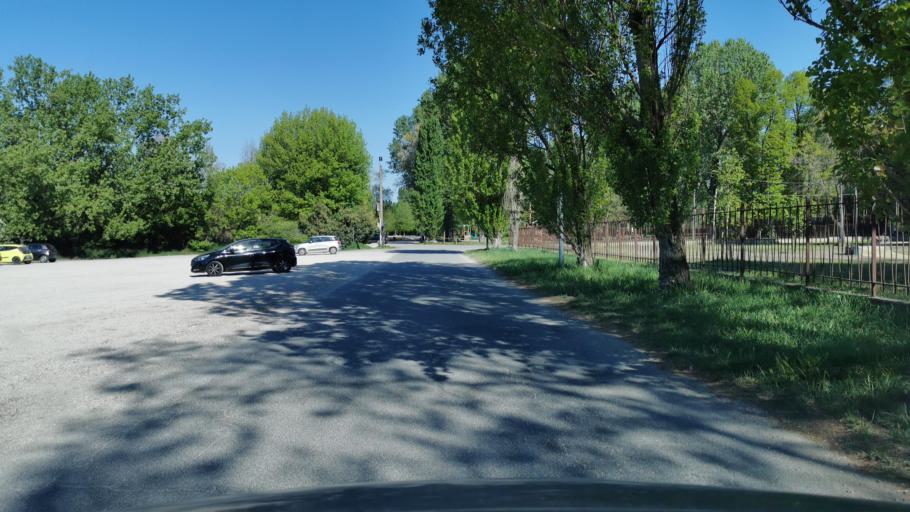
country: IT
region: Lombardy
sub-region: Provincia di Cremona
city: Cremona
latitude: 45.1223
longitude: 10.0059
